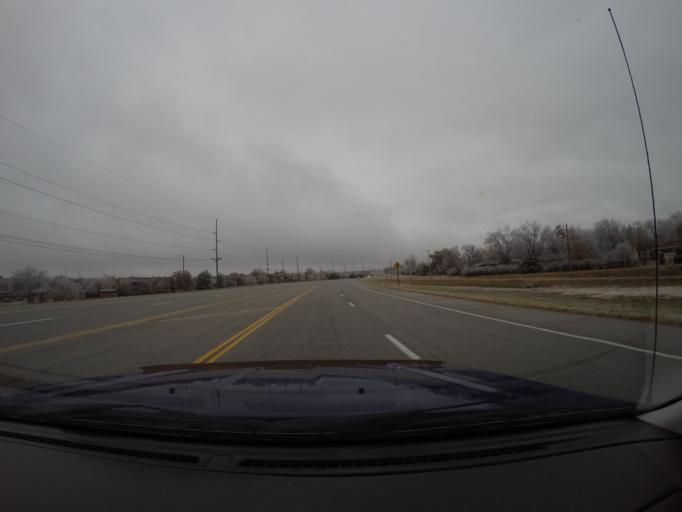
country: US
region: Kansas
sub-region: Riley County
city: Manhattan
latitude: 39.2050
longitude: -96.6166
